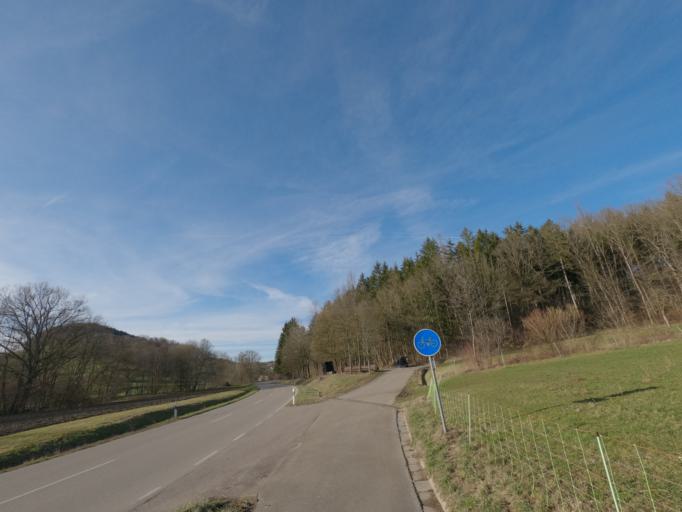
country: DE
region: Baden-Wuerttemberg
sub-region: Regierungsbezirk Stuttgart
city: Donzdorf
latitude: 48.7011
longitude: 9.8003
